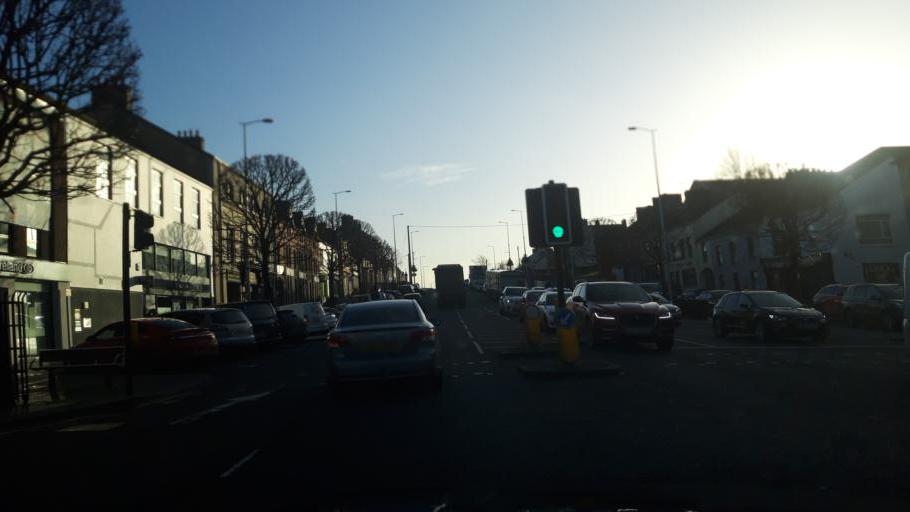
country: GB
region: Northern Ireland
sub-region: Cookstown District
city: Cookstown
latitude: 54.6460
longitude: -6.7450
